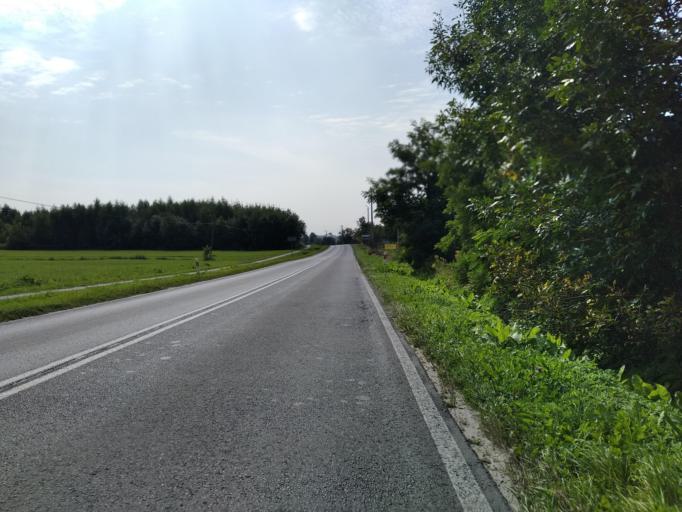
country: PL
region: Subcarpathian Voivodeship
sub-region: Powiat ropczycko-sedziszowski
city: Ostrow
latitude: 50.1032
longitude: 21.5934
